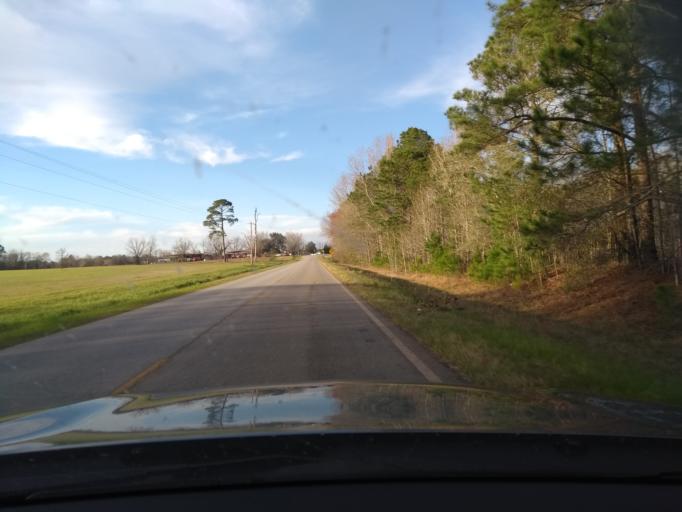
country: US
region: Georgia
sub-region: Bulloch County
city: Statesboro
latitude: 32.3552
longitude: -81.7712
